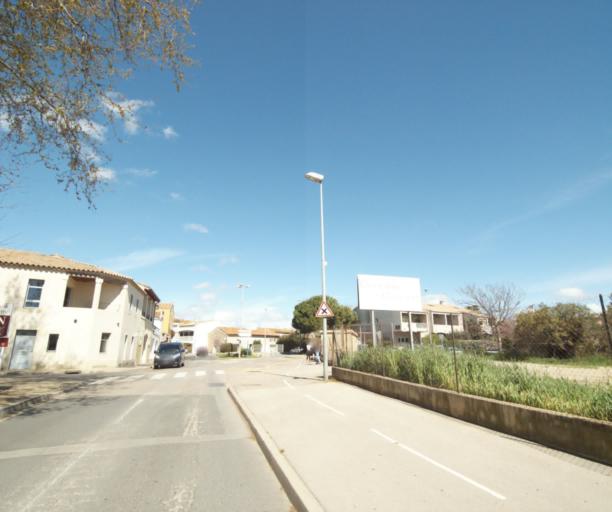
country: FR
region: Languedoc-Roussillon
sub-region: Departement de l'Herault
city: Villeneuve-les-Maguelone
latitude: 43.5329
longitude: 3.8648
